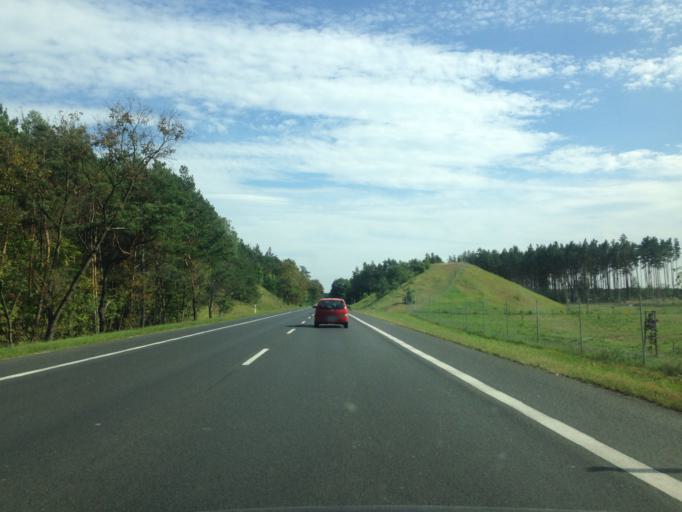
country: PL
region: Kujawsko-Pomorskie
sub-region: Powiat aleksandrowski
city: Aleksandrow Kujawski
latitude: 52.9006
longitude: 18.7255
